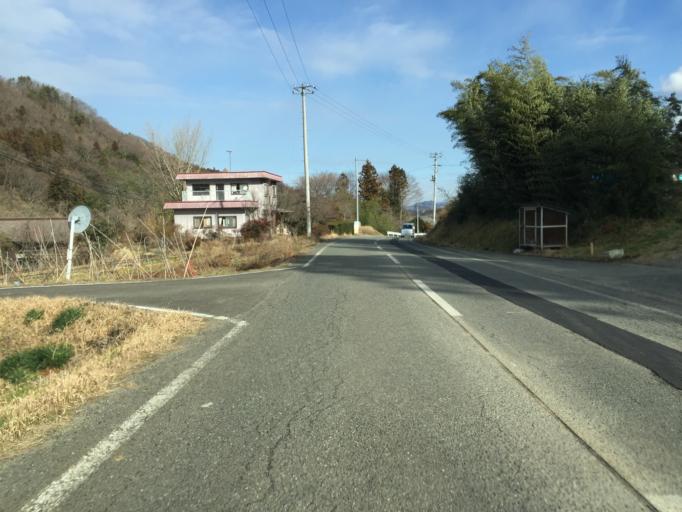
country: JP
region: Fukushima
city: Hobaramachi
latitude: 37.7387
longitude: 140.5589
